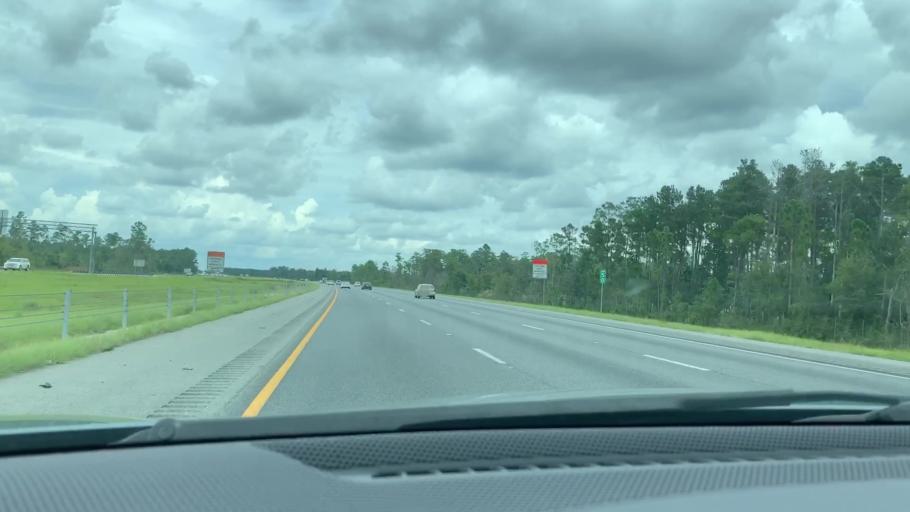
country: US
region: Georgia
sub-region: McIntosh County
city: Darien
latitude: 31.4123
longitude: -81.4442
